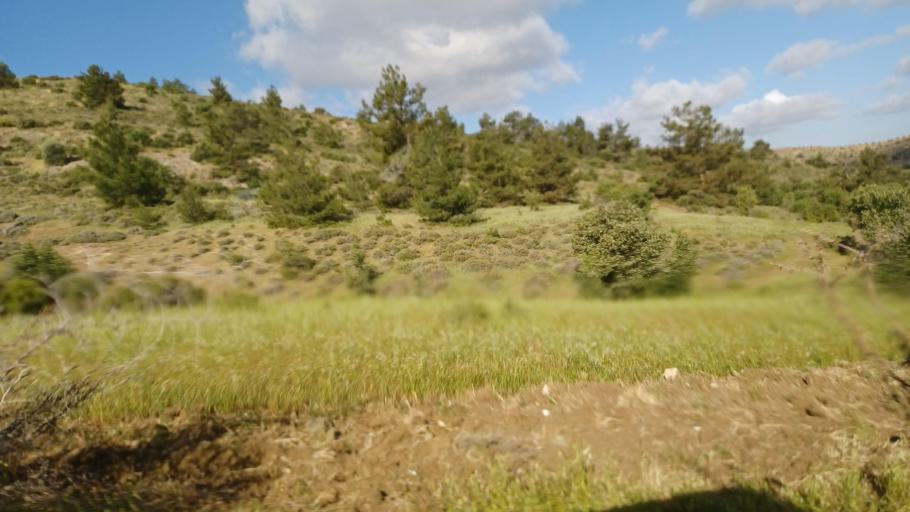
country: CY
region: Lefkosia
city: Peristerona
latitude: 35.0653
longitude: 33.0496
